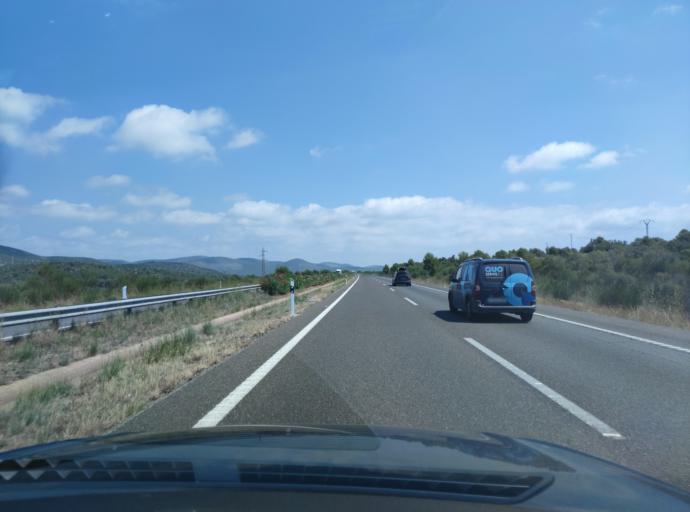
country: ES
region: Valencia
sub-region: Provincia de Castello
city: Santa Magdalena de Pulpis
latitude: 40.3355
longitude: 0.2666
